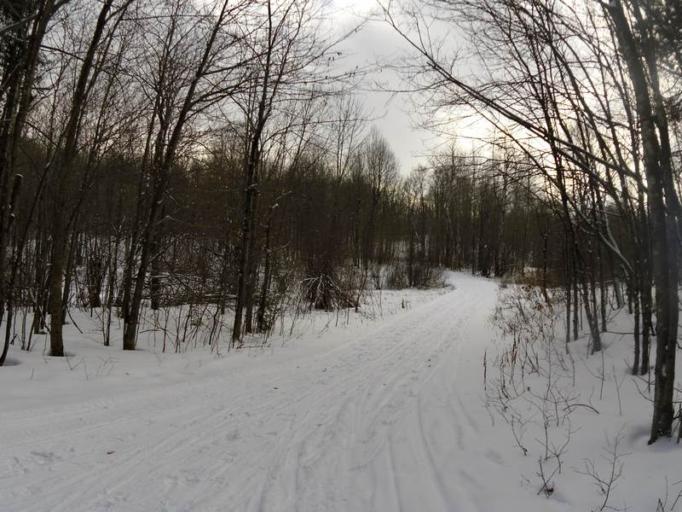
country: CA
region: Quebec
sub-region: Outaouais
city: Wakefield
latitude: 45.5212
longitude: -75.9133
